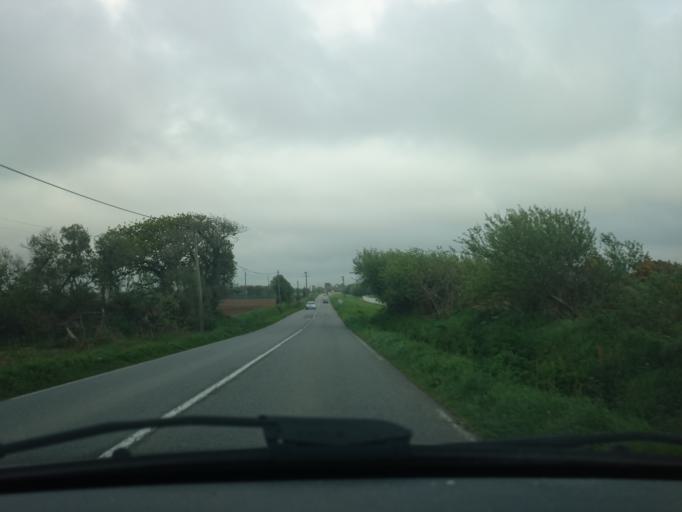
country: FR
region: Brittany
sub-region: Departement du Finistere
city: Lanrivoare
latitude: 48.4742
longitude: -4.6509
